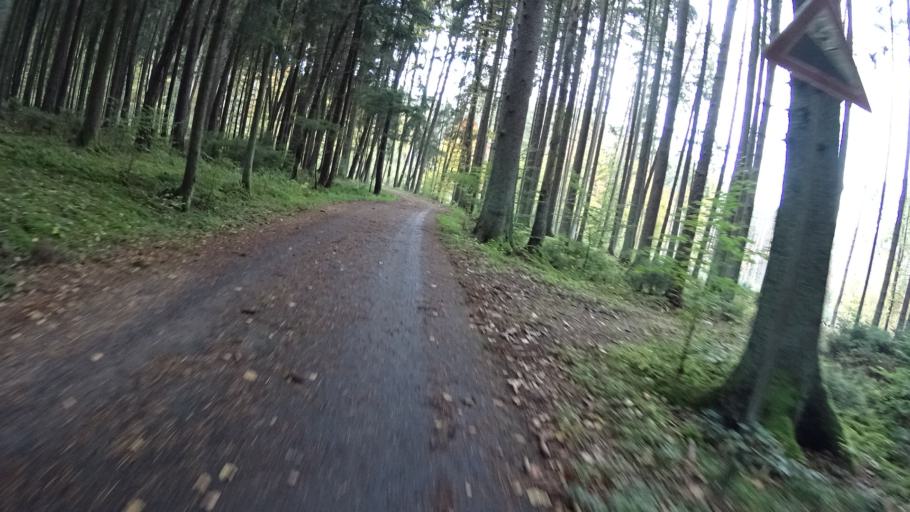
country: DE
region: Bavaria
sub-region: Upper Bavaria
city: Adelschlag
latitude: 48.8445
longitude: 11.2590
